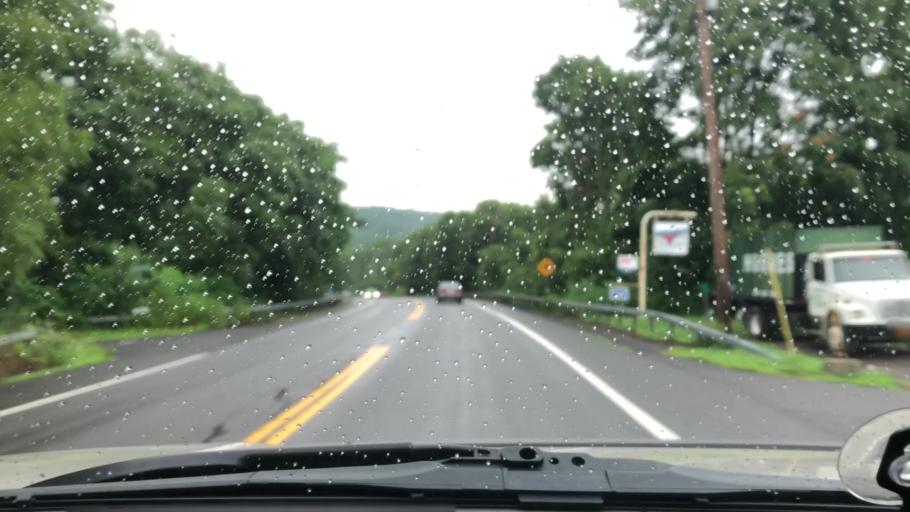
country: US
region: New York
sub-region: Ulster County
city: Saugerties
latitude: 42.1110
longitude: -73.9693
